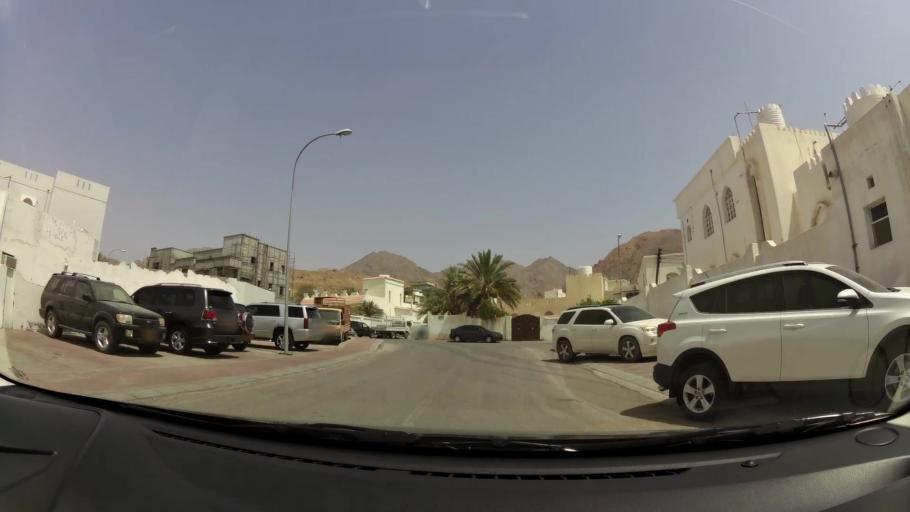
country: OM
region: Muhafazat Masqat
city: Bawshar
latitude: 23.5340
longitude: 58.3840
